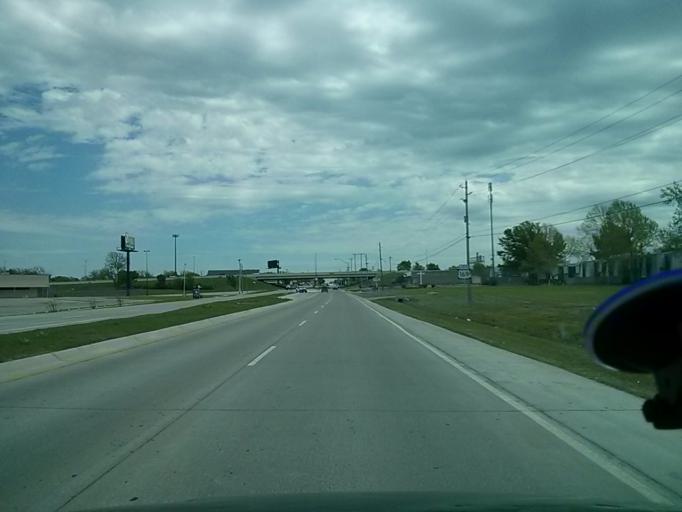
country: US
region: Oklahoma
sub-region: Tulsa County
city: Owasso
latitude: 36.1606
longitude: -95.8648
